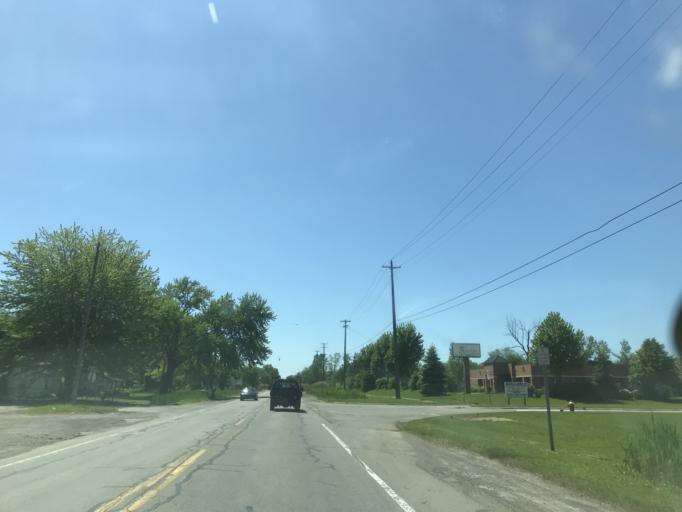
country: US
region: Michigan
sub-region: Wayne County
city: Inkster
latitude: 42.2533
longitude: -83.3314
